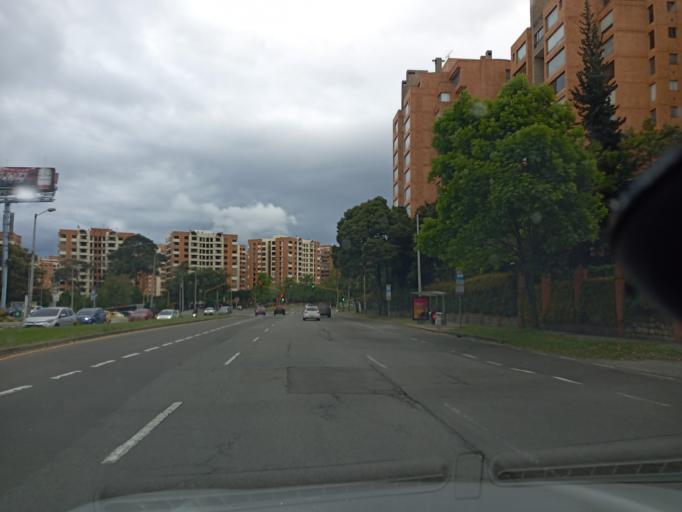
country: CO
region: Bogota D.C.
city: Barrio San Luis
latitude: 4.7107
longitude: -74.0287
